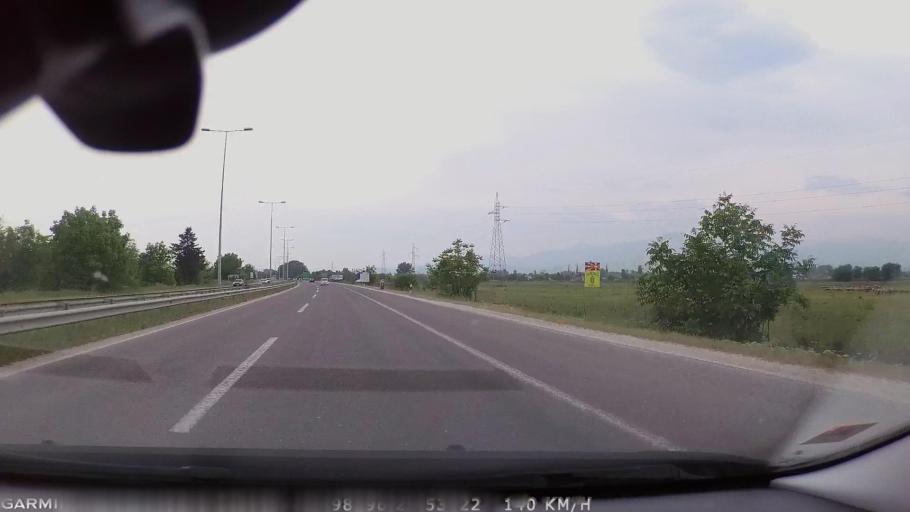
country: MK
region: Ilinden
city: Jurumleri
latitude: 41.9846
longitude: 21.5381
